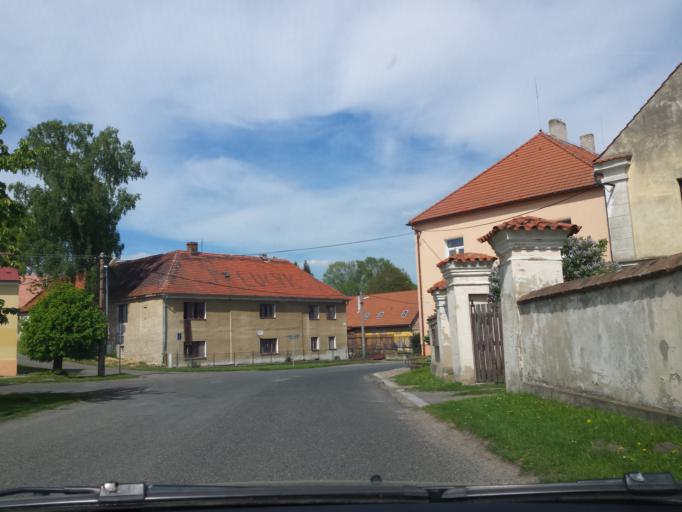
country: CZ
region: Central Bohemia
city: Dolni Berkovice
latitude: 50.4120
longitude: 14.5338
